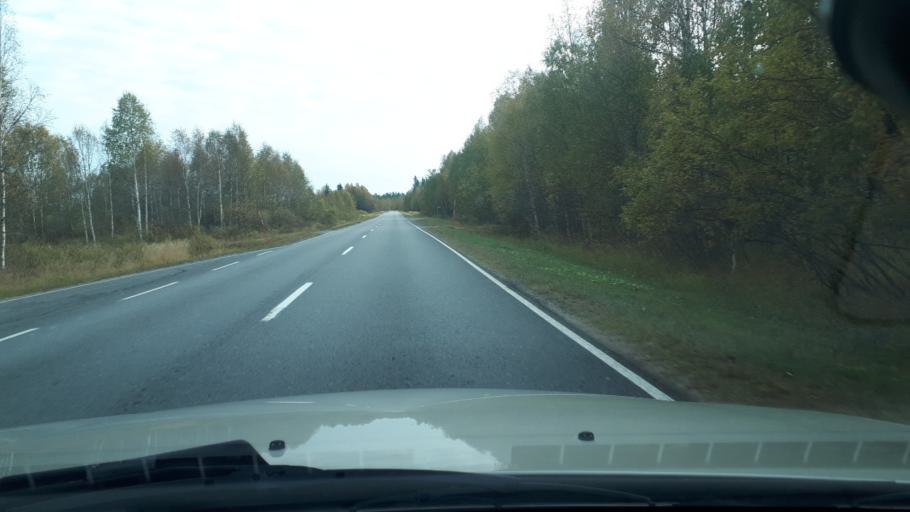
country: FI
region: Lapland
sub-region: Rovaniemi
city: Ranua
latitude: 65.9613
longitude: 26.0505
